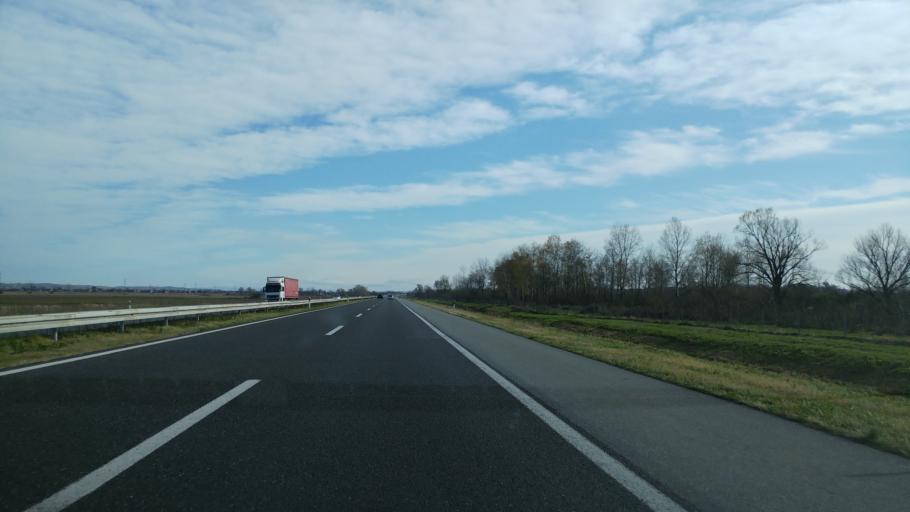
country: HR
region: Sisacko-Moslavacka
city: Repusnica
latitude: 45.4871
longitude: 16.7001
